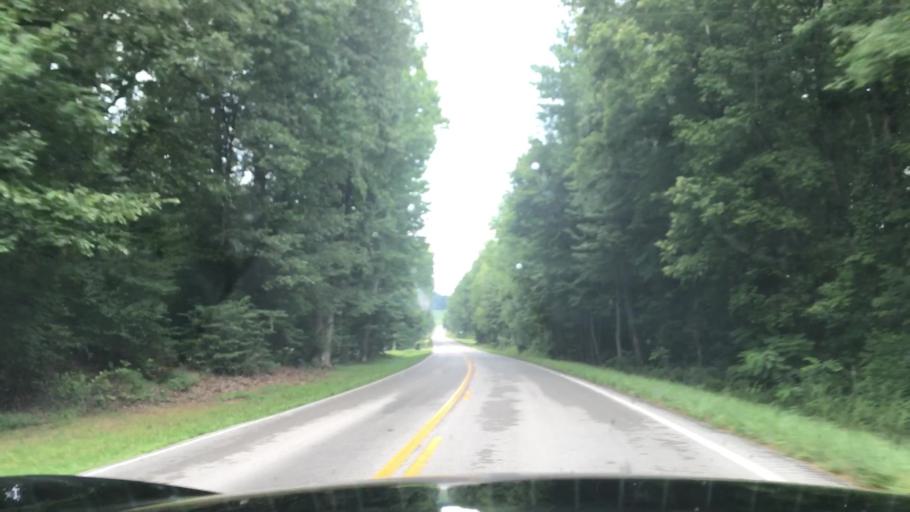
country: US
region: Kentucky
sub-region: Butler County
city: Morgantown
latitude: 37.1748
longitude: -86.8394
